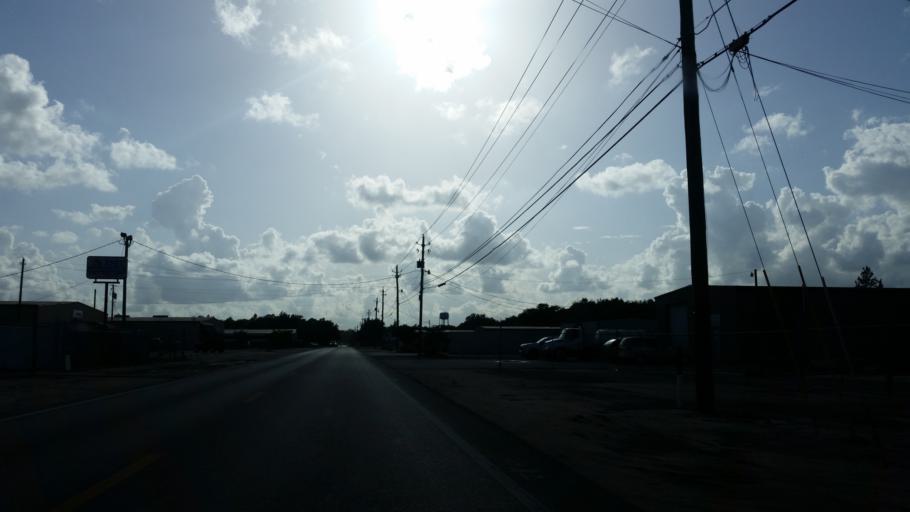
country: US
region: Florida
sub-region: Santa Rosa County
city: Bagdad
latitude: 30.5867
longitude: -87.0772
